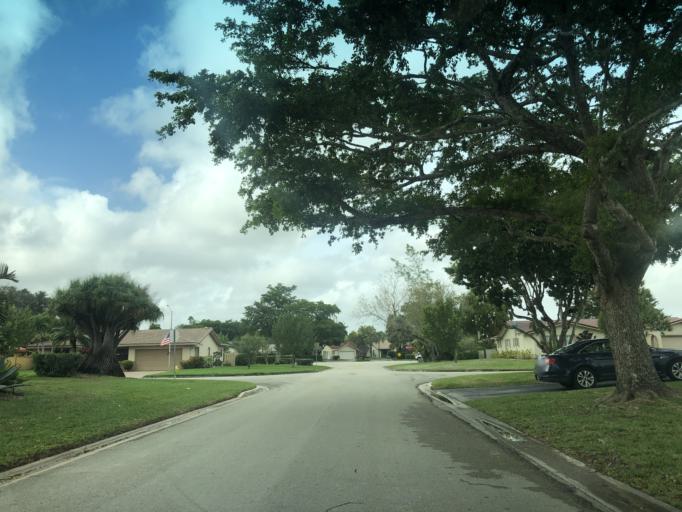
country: US
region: Florida
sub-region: Broward County
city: Margate
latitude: 26.2513
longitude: -80.2391
